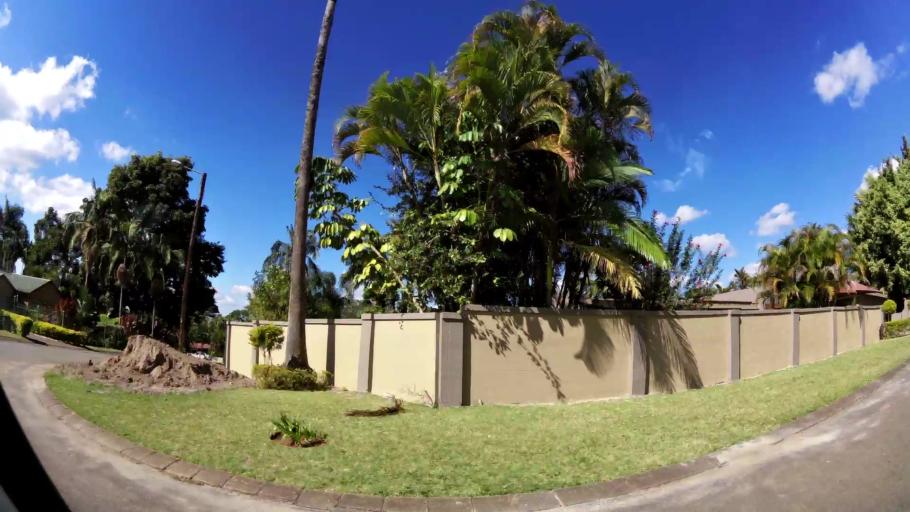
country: ZA
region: Limpopo
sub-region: Mopani District Municipality
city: Tzaneen
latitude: -23.8182
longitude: 30.1465
